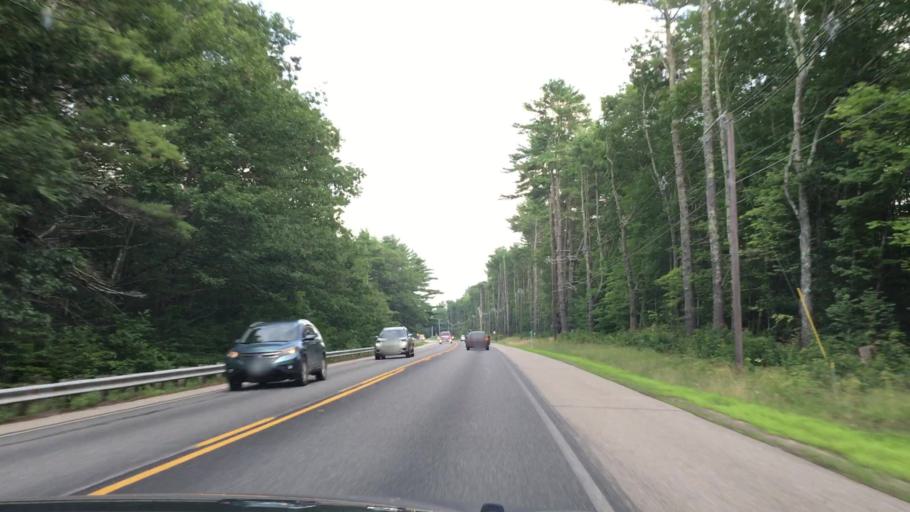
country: US
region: New Hampshire
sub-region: Strafford County
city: Farmington
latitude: 43.3792
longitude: -71.0669
